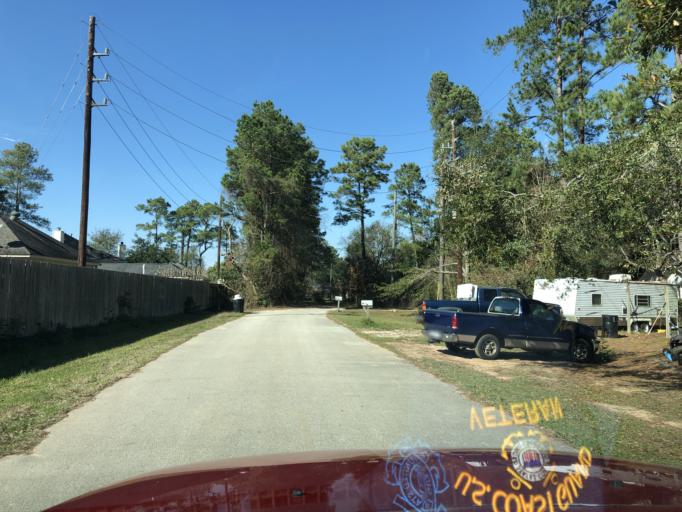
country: US
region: Texas
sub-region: Harris County
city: Tomball
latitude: 30.0328
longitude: -95.5436
